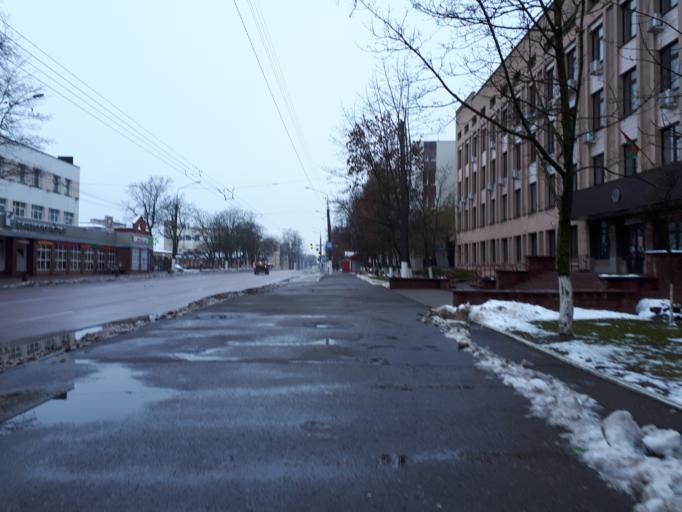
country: BY
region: Vitebsk
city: Vitebsk
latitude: 55.1871
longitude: 30.2185
